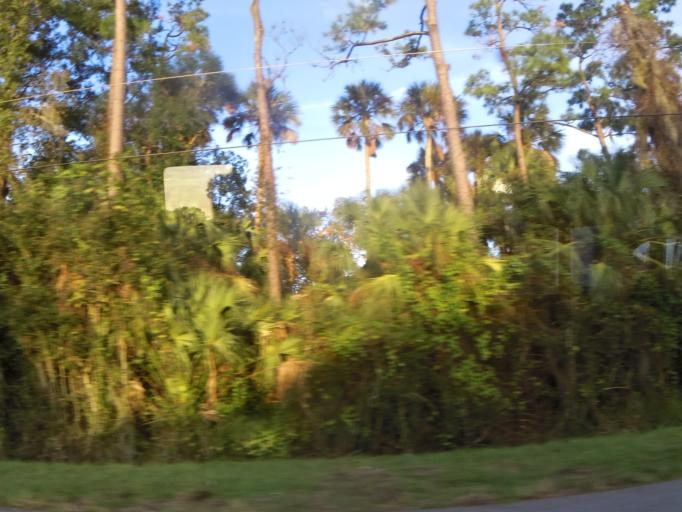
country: US
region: Florida
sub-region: Saint Johns County
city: Palm Valley
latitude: 30.1382
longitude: -81.3871
